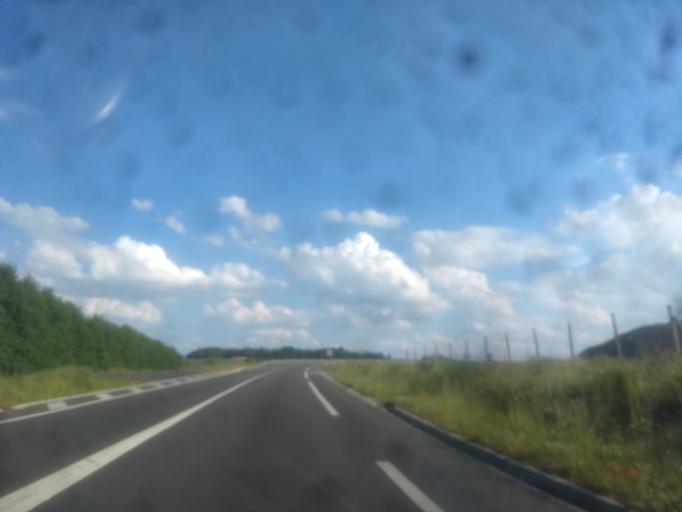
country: FR
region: Nord-Pas-de-Calais
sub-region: Departement du Pas-de-Calais
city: Dainville
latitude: 50.2689
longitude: 2.7124
